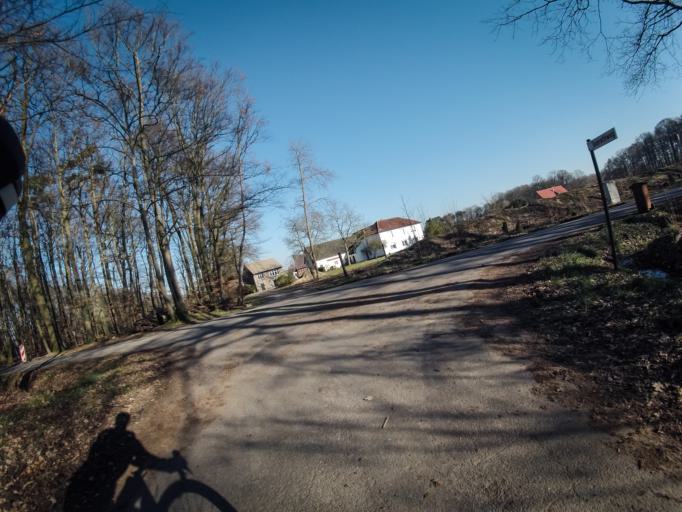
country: DE
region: North Rhine-Westphalia
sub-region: Regierungsbezirk Munster
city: Lotte
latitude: 52.2704
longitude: 7.9399
